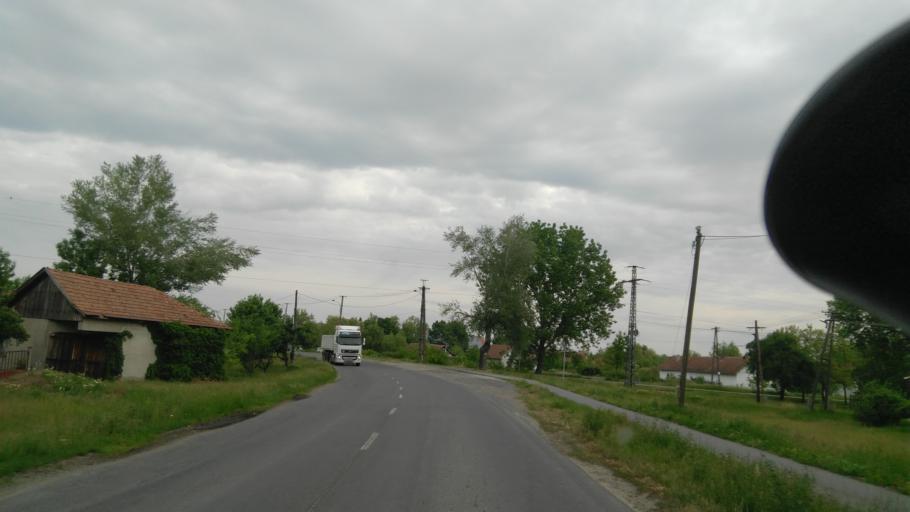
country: HU
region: Bekes
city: Veszto
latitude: 46.9083
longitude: 21.2581
